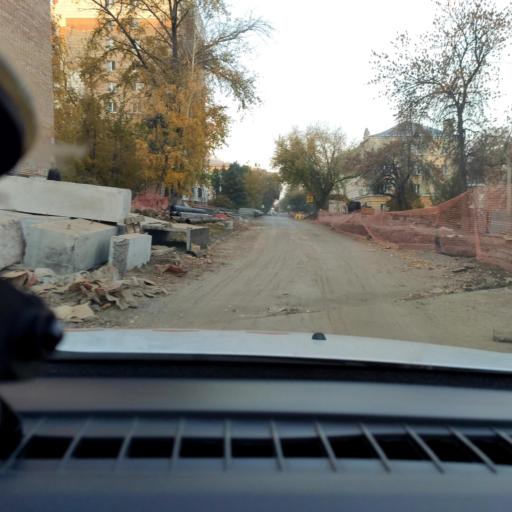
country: RU
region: Samara
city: Samara
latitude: 53.2152
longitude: 50.1586
